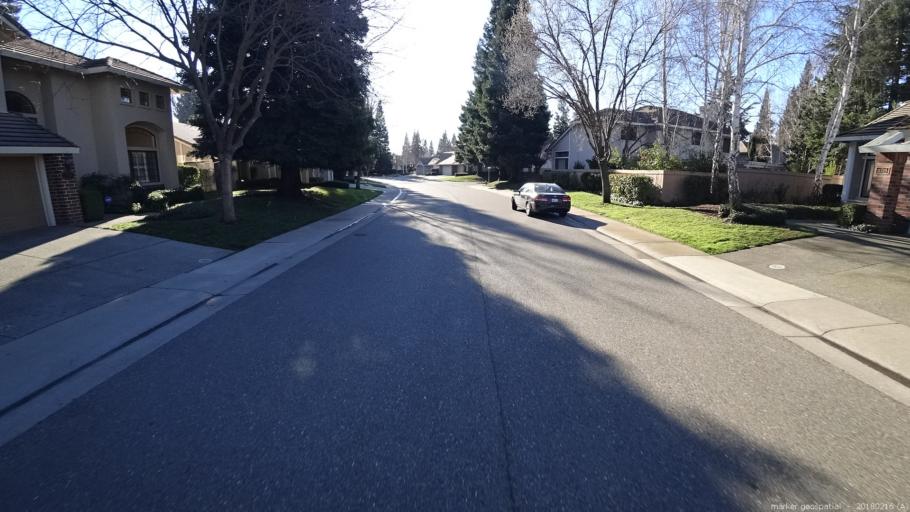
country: US
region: California
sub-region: Sacramento County
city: Gold River
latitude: 38.6273
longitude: -121.2368
